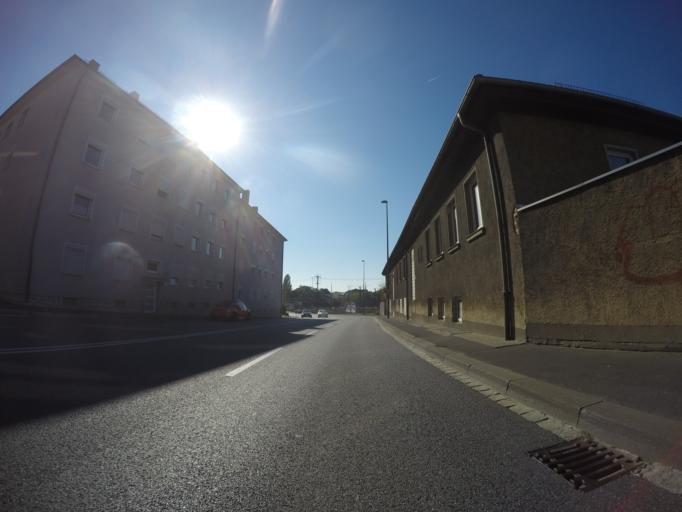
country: DE
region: Bavaria
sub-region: Regierungsbezirk Unterfranken
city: Wuerzburg
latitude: 49.8030
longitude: 9.9405
